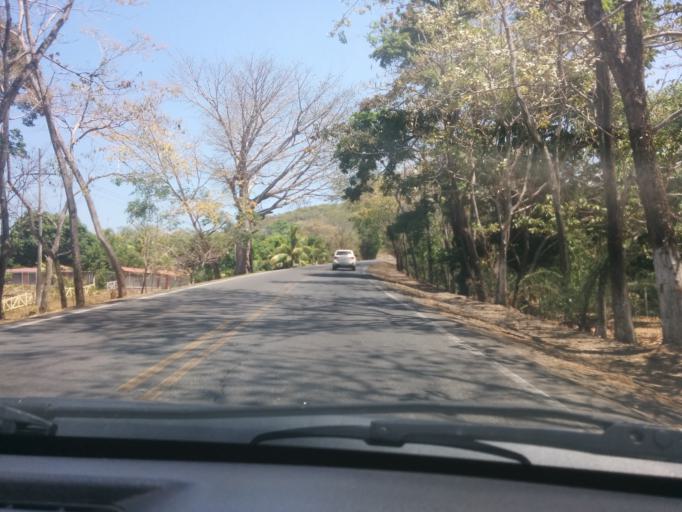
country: CR
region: Puntarenas
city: Esparza
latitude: 10.0100
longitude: -84.6184
